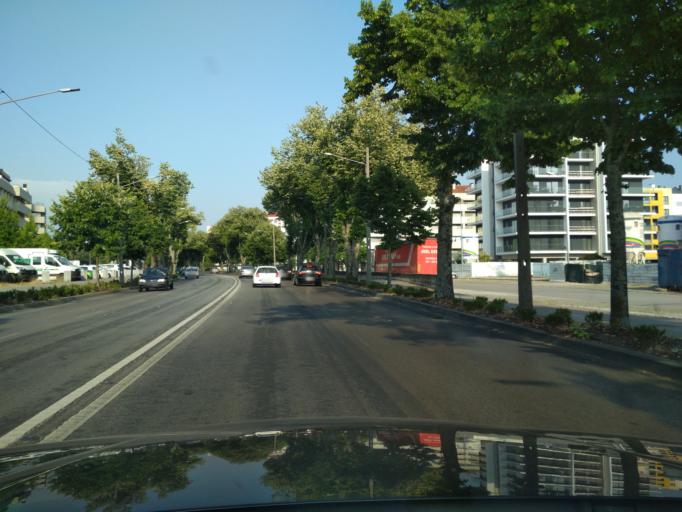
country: PT
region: Viseu
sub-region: Viseu
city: Viseu
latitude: 40.6488
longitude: -7.9163
